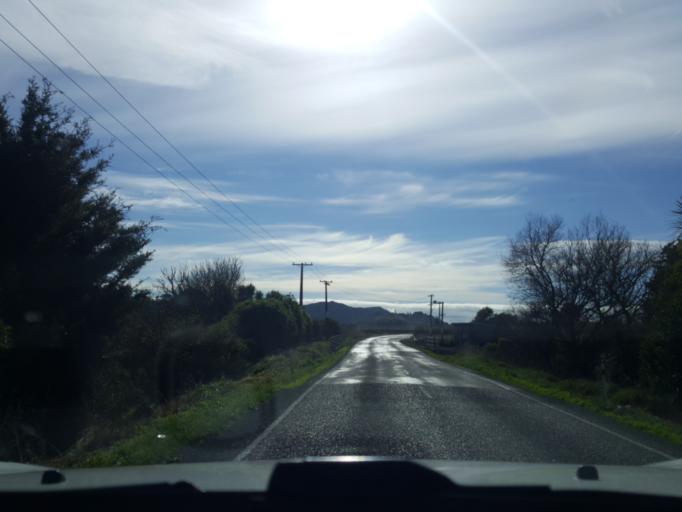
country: NZ
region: Waikato
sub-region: Waikato District
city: Ngaruawahia
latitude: -37.6071
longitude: 175.1978
